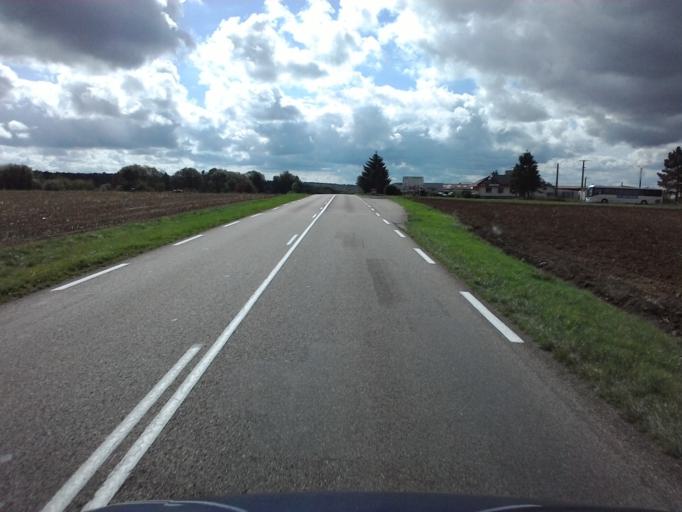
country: FR
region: Lorraine
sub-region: Departement de Meurthe-et-Moselle
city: Colombey-les-Belles
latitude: 48.4514
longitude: 5.8039
